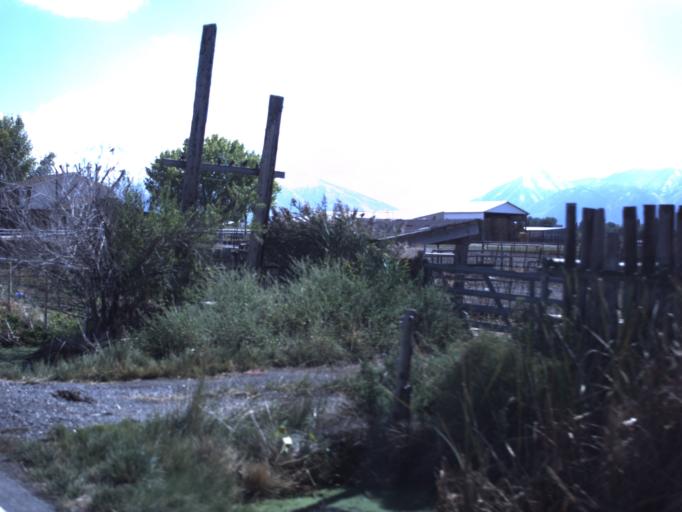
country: US
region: Utah
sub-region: Utah County
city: Benjamin
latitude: 40.1583
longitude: -111.7055
